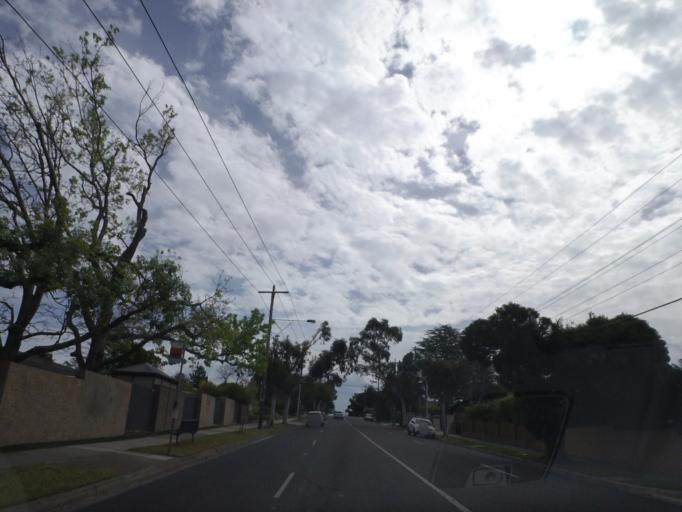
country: AU
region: Victoria
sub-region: Monash
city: Ashwood
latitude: -37.8664
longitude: 145.0976
